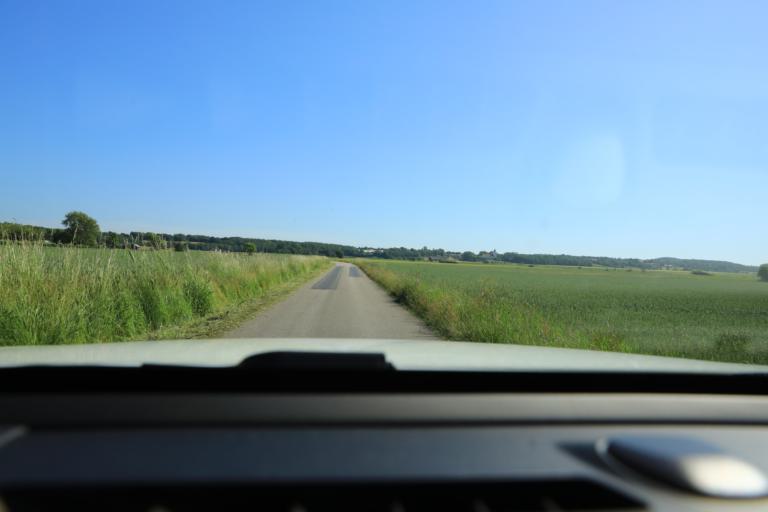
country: SE
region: Halland
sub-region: Varbergs Kommun
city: Veddige
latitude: 57.1741
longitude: 12.3151
